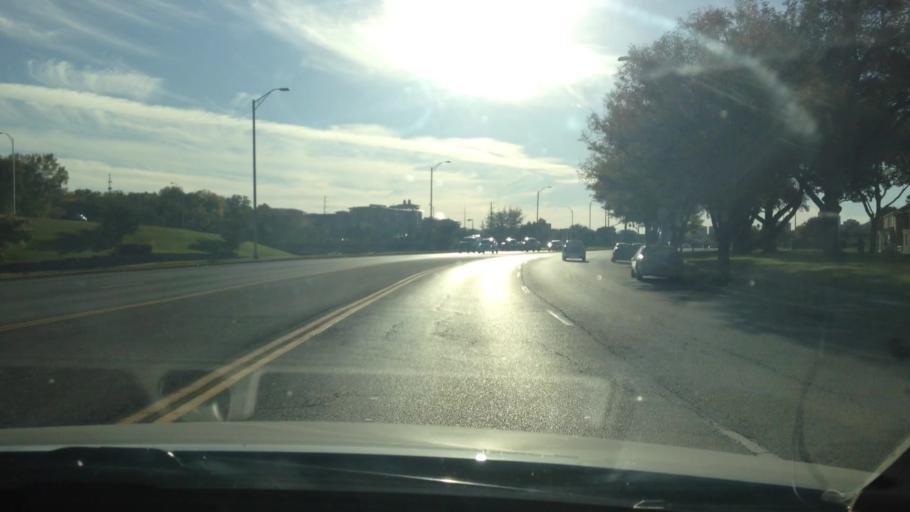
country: US
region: Kansas
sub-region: Johnson County
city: Westwood
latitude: 39.0424
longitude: -94.5654
